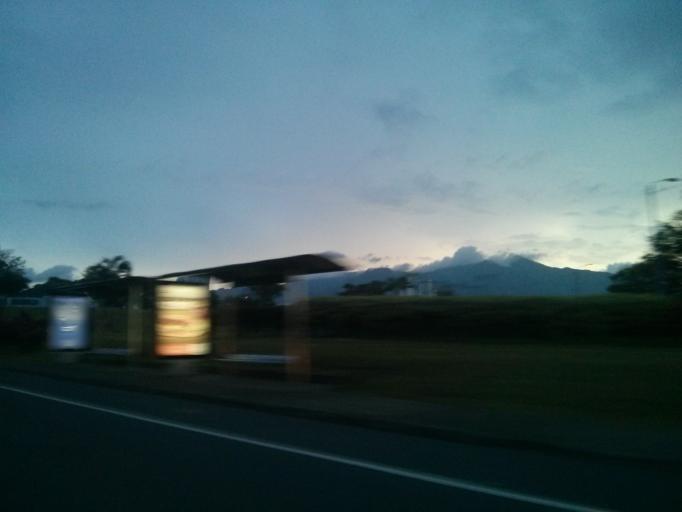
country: CR
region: San Jose
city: Colima
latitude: 9.9472
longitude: -84.1098
